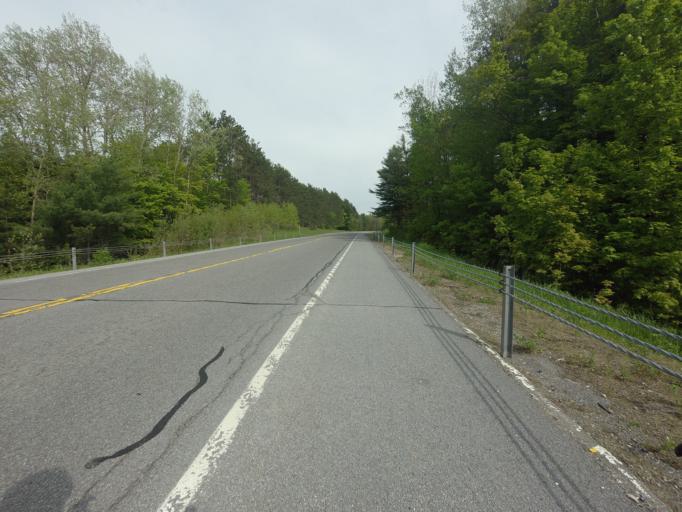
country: US
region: New York
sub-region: St. Lawrence County
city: Gouverneur
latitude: 44.2857
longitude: -75.2085
